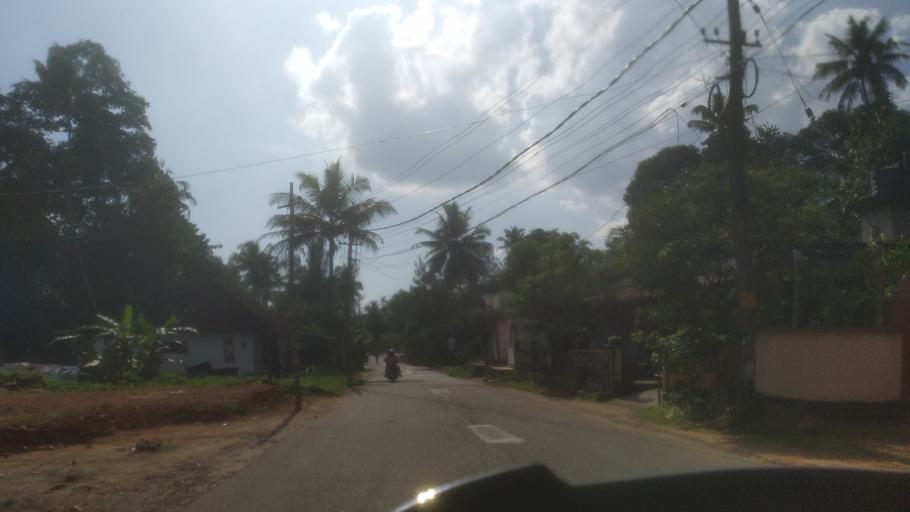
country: IN
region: Kerala
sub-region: Ernakulam
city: Muvattupula
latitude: 9.9997
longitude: 76.6295
